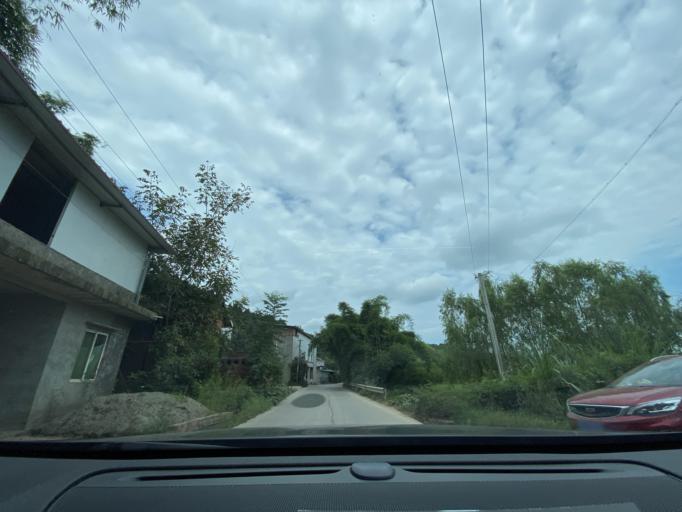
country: CN
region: Sichuan
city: Jiancheng
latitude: 30.4406
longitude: 104.5408
